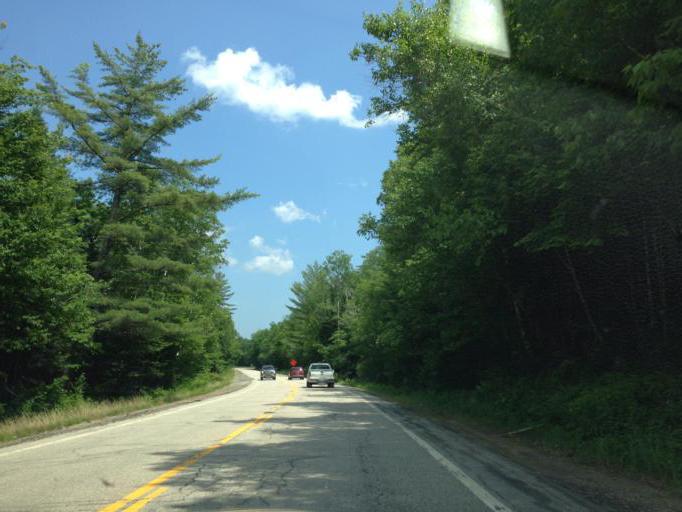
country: US
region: New Hampshire
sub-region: Carroll County
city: Tamworth
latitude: 43.9971
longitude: -71.3890
